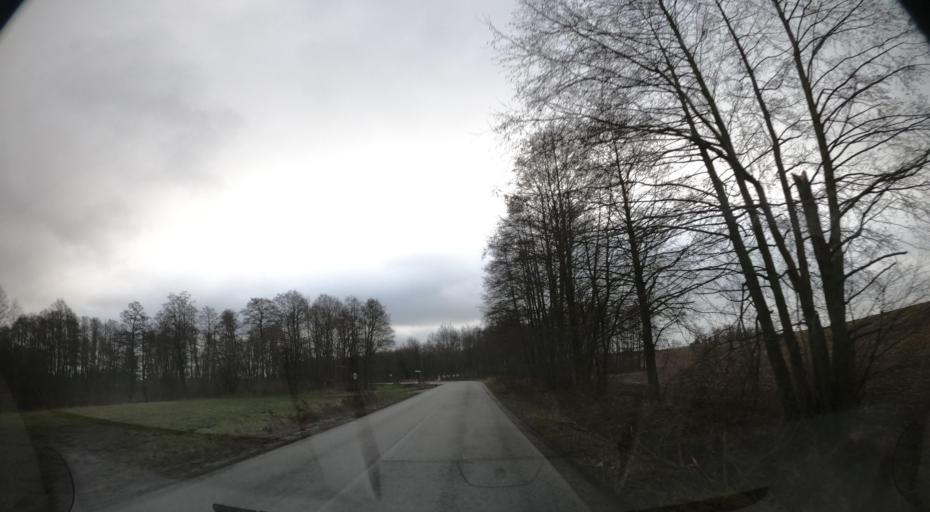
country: PL
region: Kujawsko-Pomorskie
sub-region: Powiat nakielski
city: Sadki
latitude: 53.1885
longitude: 17.3948
